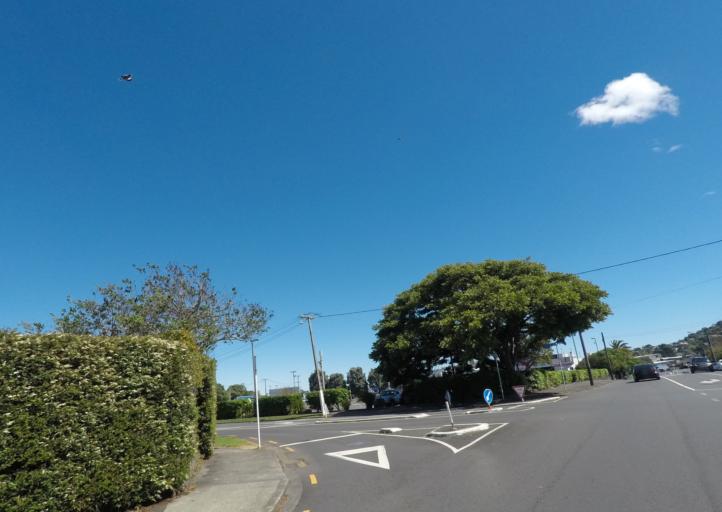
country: NZ
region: Auckland
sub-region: Auckland
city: Auckland
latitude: -36.8806
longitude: 174.7339
